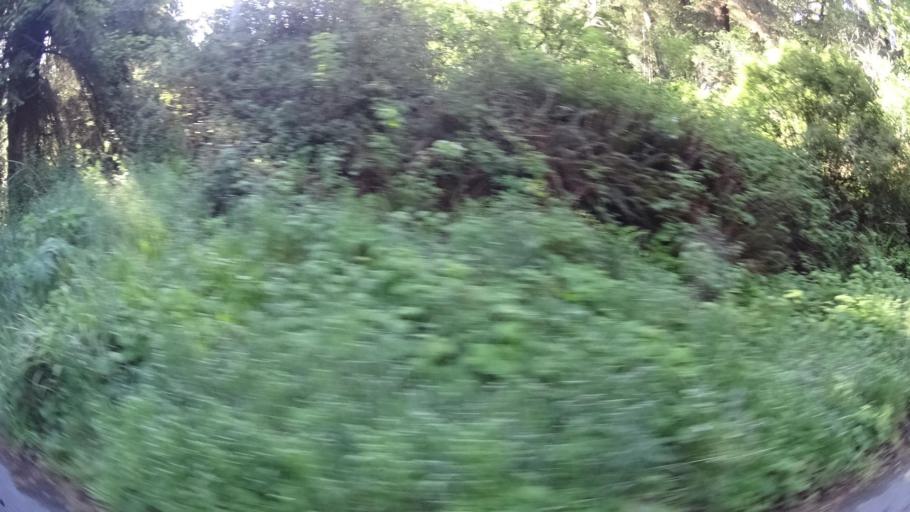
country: US
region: California
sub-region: Humboldt County
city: Westhaven-Moonstone
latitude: 41.1356
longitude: -124.1506
